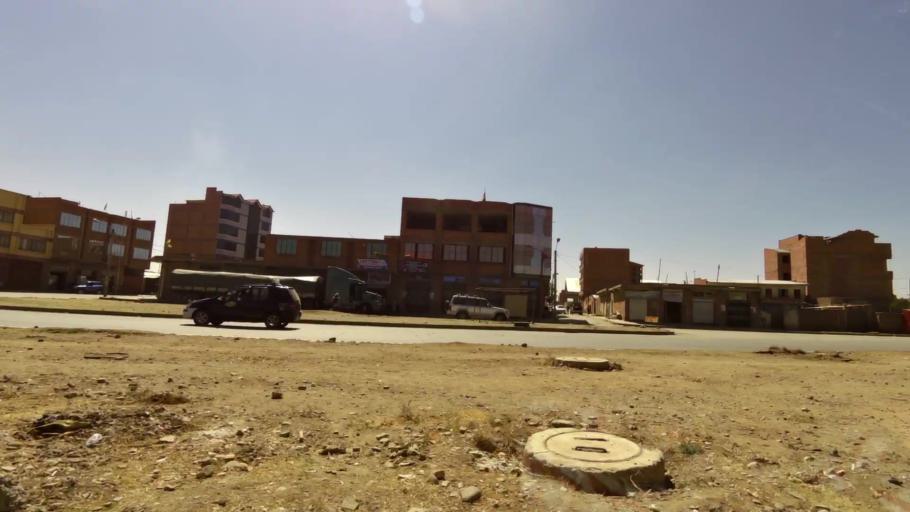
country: BO
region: La Paz
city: La Paz
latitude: -16.5509
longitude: -68.1881
